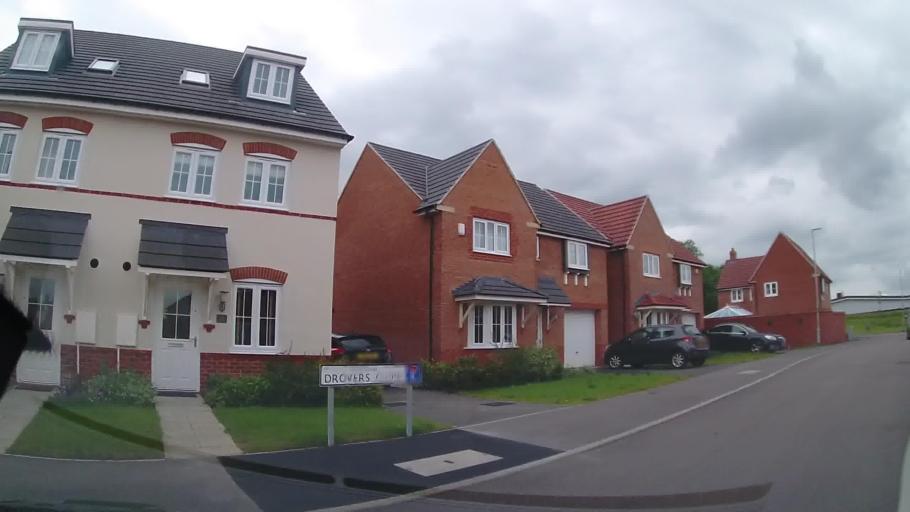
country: GB
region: England
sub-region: Leicestershire
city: Glenfield
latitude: 52.6439
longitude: -1.2115
